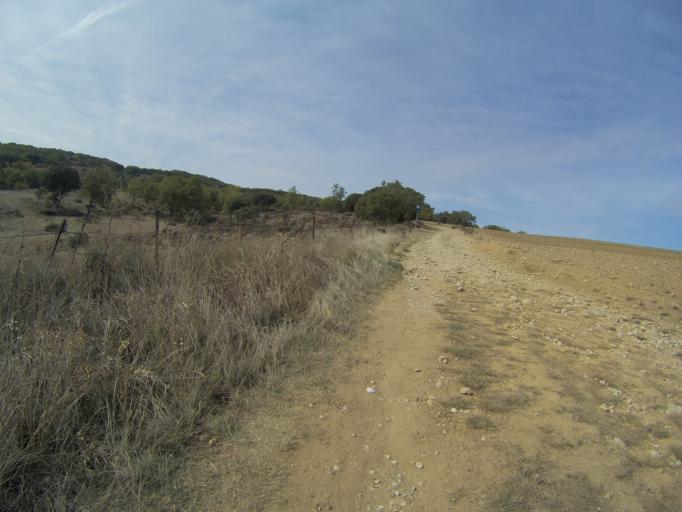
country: ES
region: Castille and Leon
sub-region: Provincia de Burgos
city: Atapuerca
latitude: 42.3794
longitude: -3.5223
